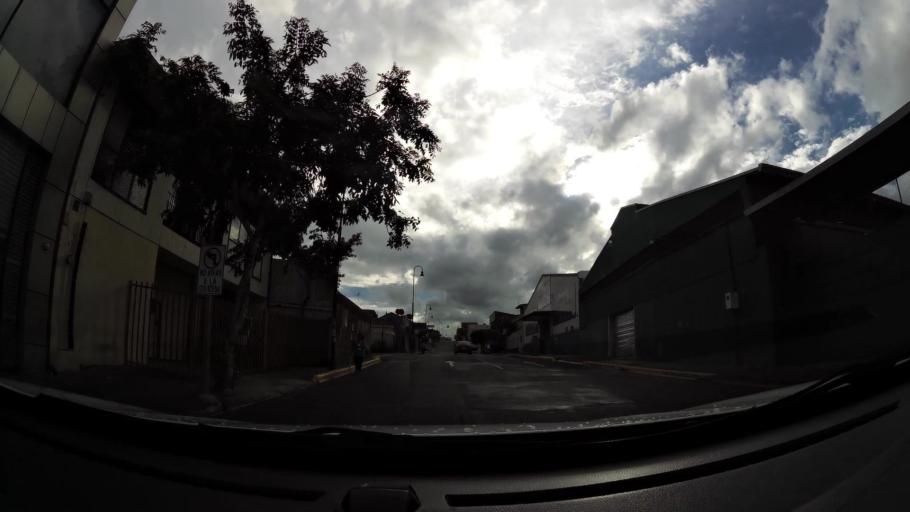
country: CR
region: San Jose
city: San Jose
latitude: 9.9388
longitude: -84.0857
